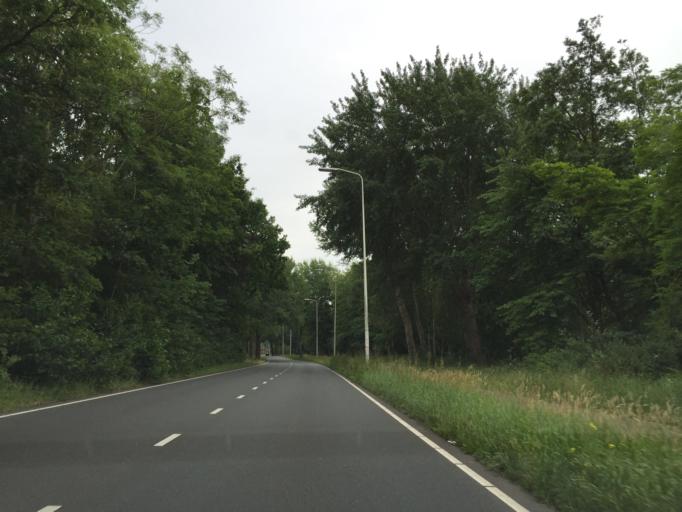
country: NL
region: South Holland
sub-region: Gemeente Westland
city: Poeldijk
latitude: 52.0501
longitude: 4.2304
